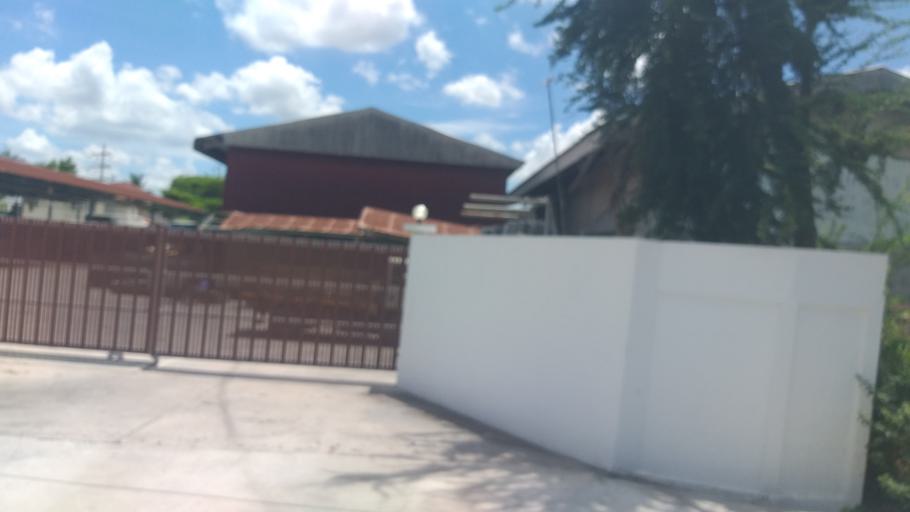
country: TH
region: Nakhon Nayok
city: Ban Na
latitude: 14.2661
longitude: 101.0655
